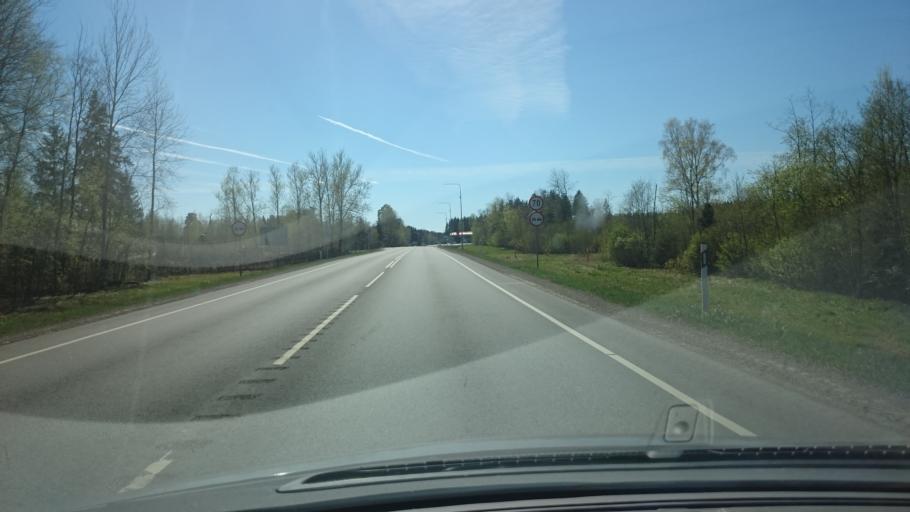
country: EE
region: Ida-Virumaa
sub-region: Johvi vald
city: Johvi
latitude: 59.3648
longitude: 27.4698
